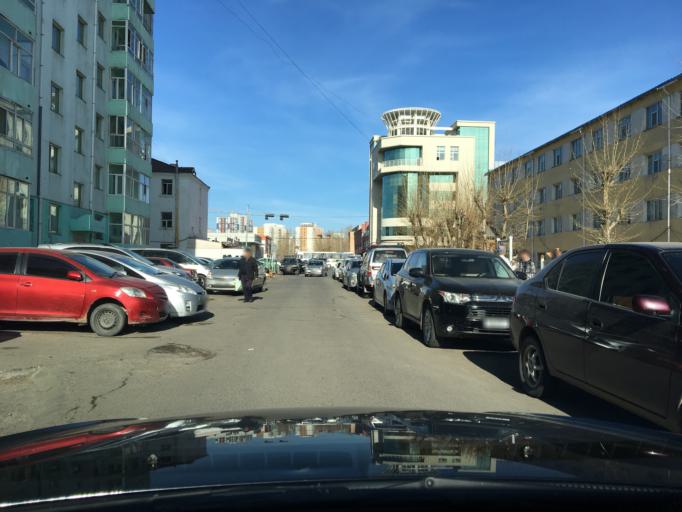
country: MN
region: Ulaanbaatar
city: Ulaanbaatar
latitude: 47.8972
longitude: 106.8907
